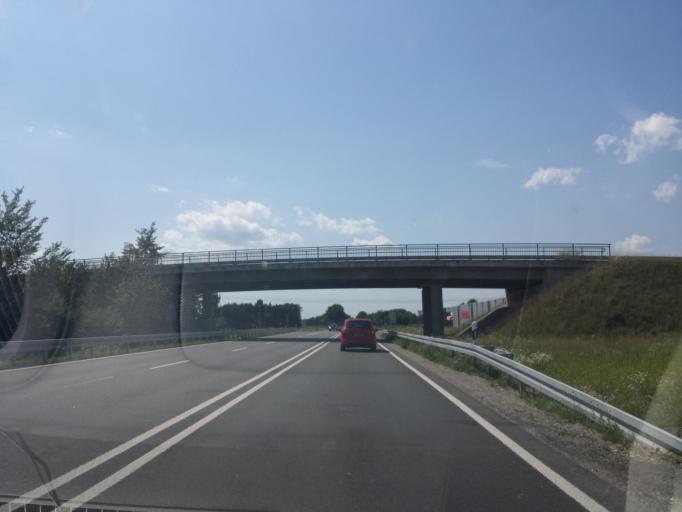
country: DE
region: Bavaria
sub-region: Upper Bavaria
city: Vohburg an der Donau
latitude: 48.7374
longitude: 11.6302
